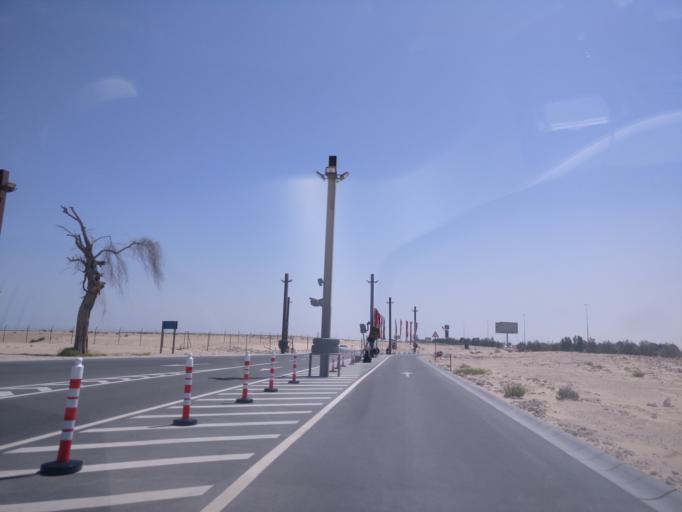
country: AE
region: Dubai
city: Dubai
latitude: 24.9136
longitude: 54.9622
